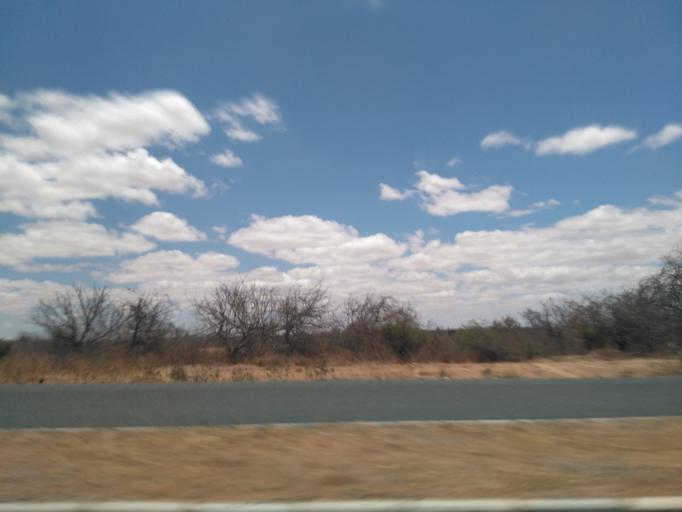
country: TZ
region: Dodoma
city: Kisasa
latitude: -6.1690
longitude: 35.8446
